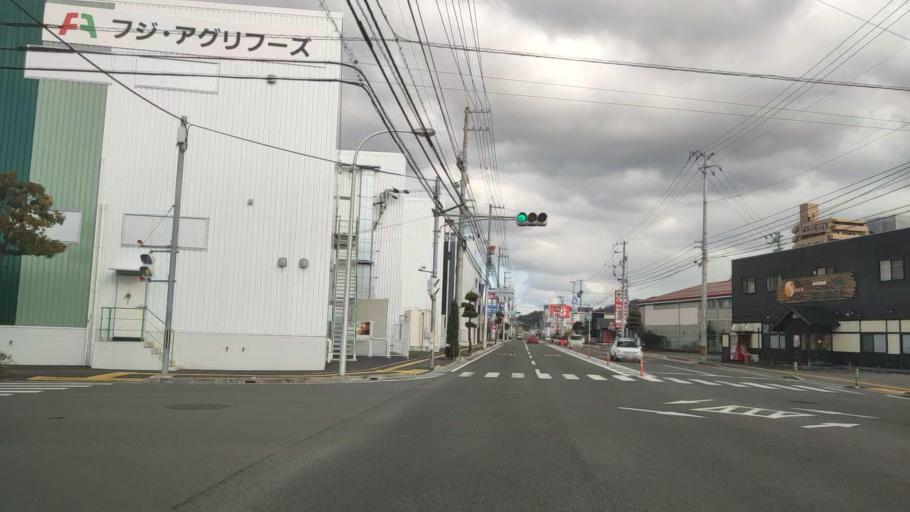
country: JP
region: Ehime
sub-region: Shikoku-chuo Shi
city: Matsuyama
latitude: 33.8609
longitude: 132.7493
